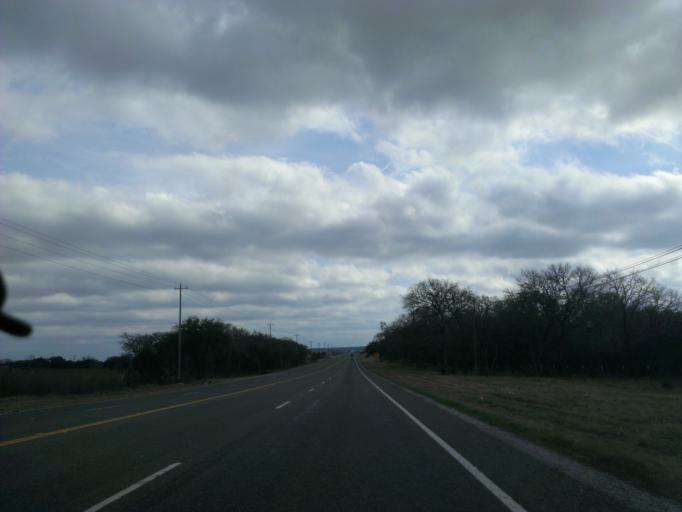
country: US
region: Texas
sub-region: Burnet County
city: Marble Falls
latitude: 30.4763
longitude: -98.1881
